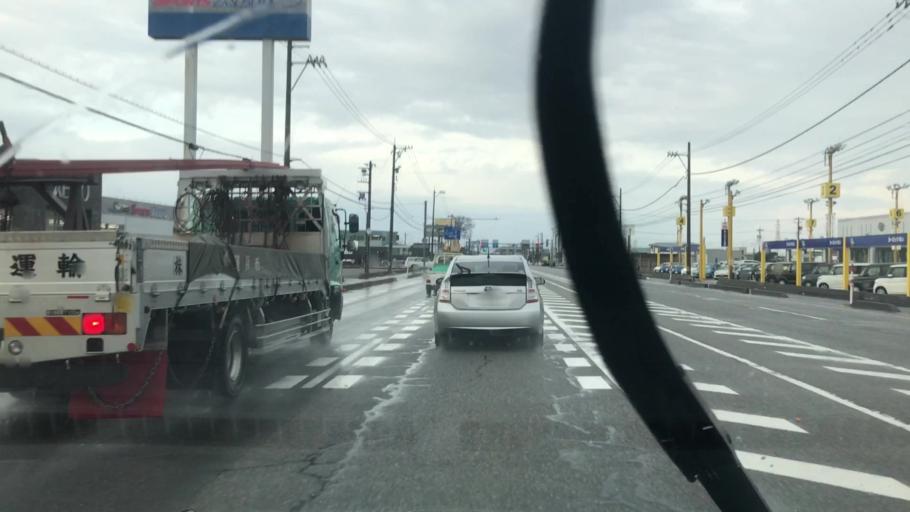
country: JP
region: Toyama
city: Toyama-shi
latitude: 36.6403
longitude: 137.2094
